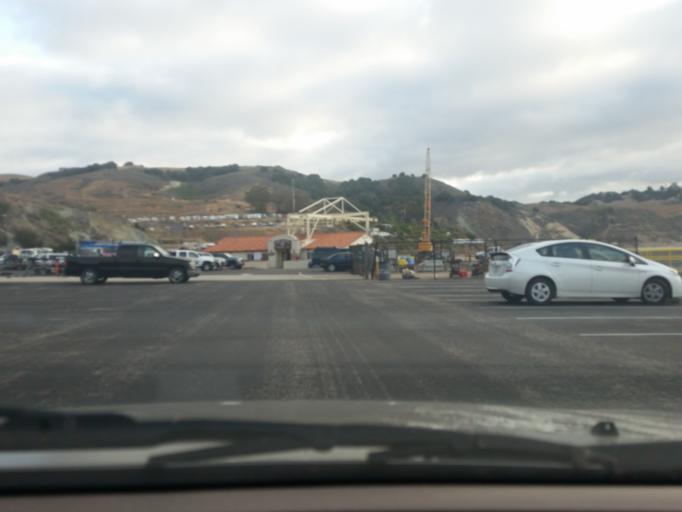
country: US
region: California
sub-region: San Luis Obispo County
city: Avila Beach
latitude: 35.1714
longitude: -120.7560
